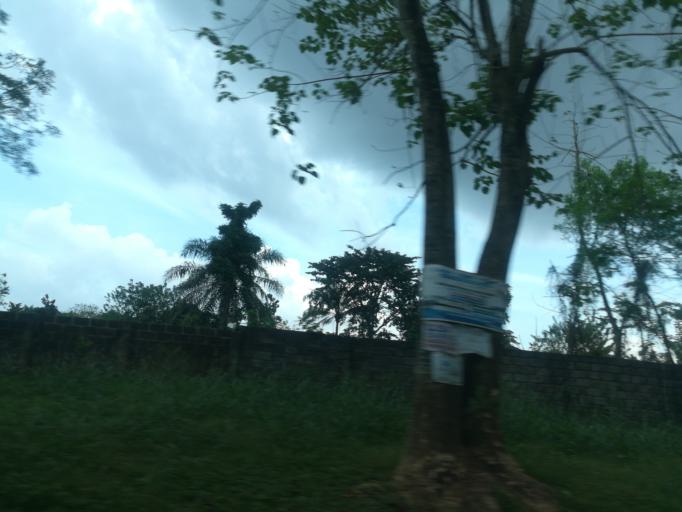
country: NG
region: Oyo
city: Ibadan
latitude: 7.4361
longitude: 3.8860
